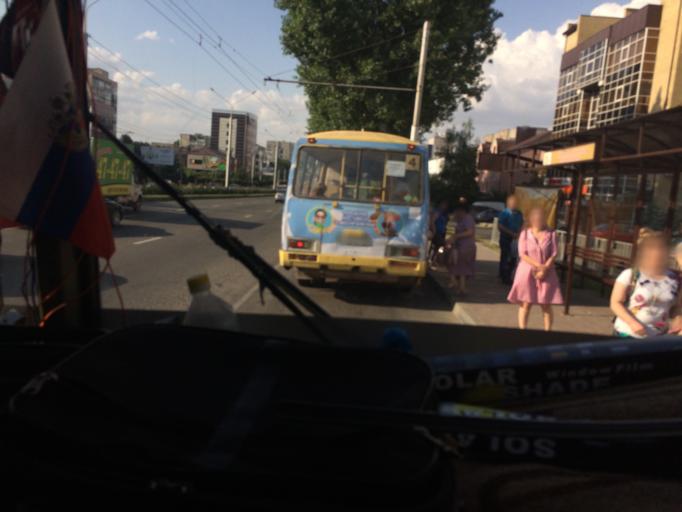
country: RU
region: Stavropol'skiy
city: Stavropol'
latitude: 45.0157
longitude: 41.9316
